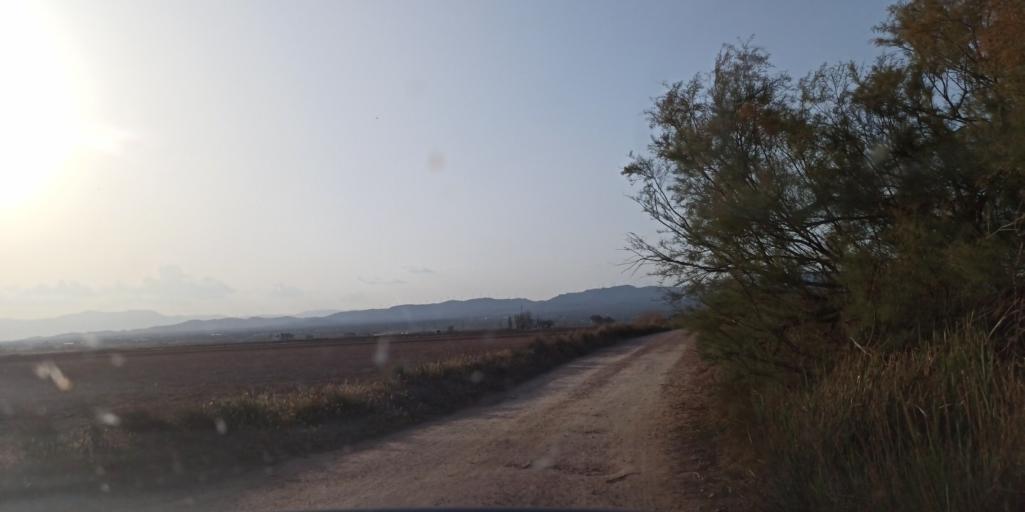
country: ES
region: Catalonia
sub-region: Provincia de Tarragona
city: L'Ampolla
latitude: 40.7792
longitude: 0.7173
